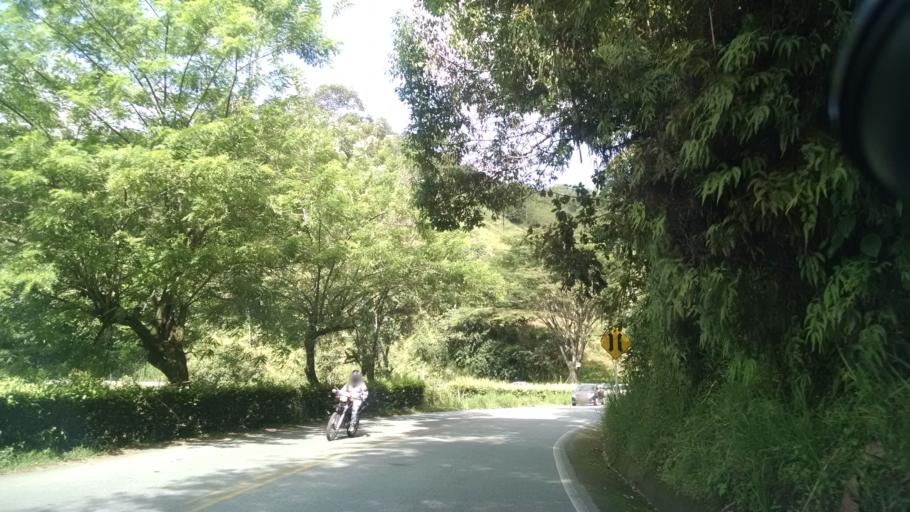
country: CO
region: Antioquia
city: Santo Domingo
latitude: 6.5280
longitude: -75.2362
